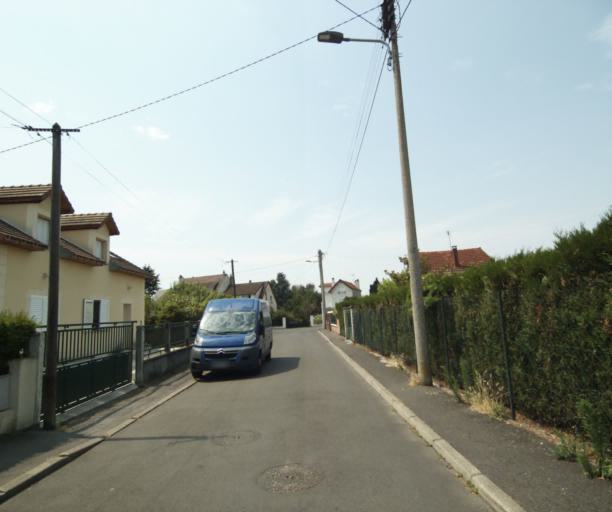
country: FR
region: Ile-de-France
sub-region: Departement des Yvelines
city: Conflans-Sainte-Honorine
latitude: 48.9966
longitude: 2.1070
